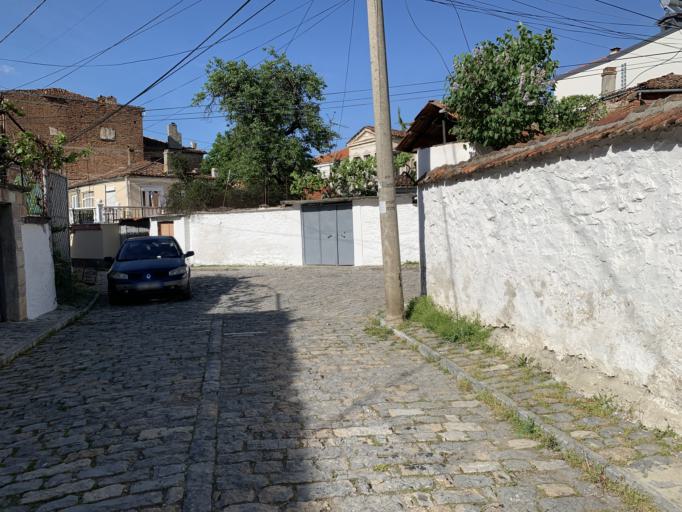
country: AL
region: Korce
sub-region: Rrethi i Korces
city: Korce
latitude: 40.6148
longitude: 20.7832
